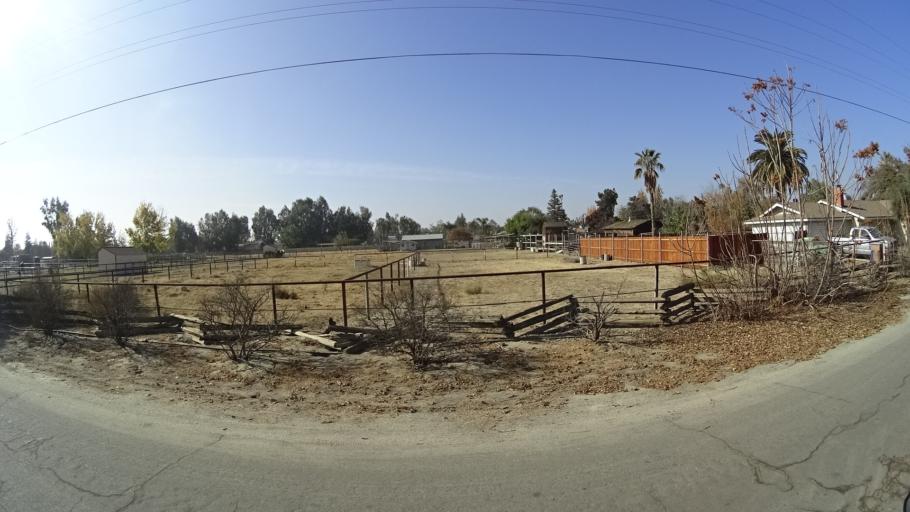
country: US
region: California
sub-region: Kern County
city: Rosedale
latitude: 35.3628
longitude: -119.1655
